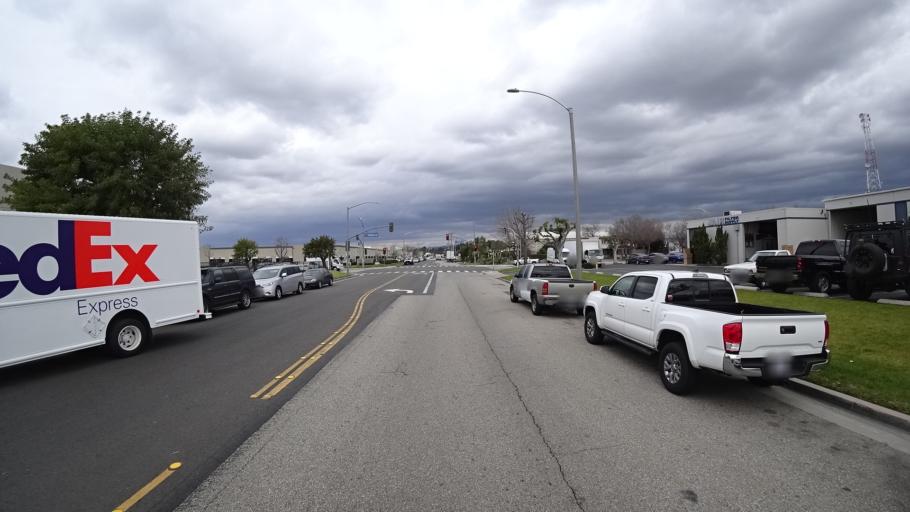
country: US
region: California
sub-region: Orange County
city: Placentia
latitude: 33.8559
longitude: -117.8658
